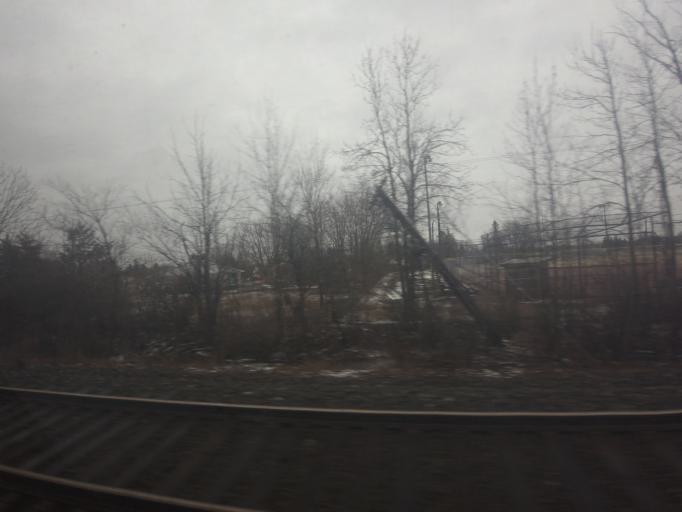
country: CA
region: Ontario
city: Kingston
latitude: 44.2277
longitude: -76.6388
